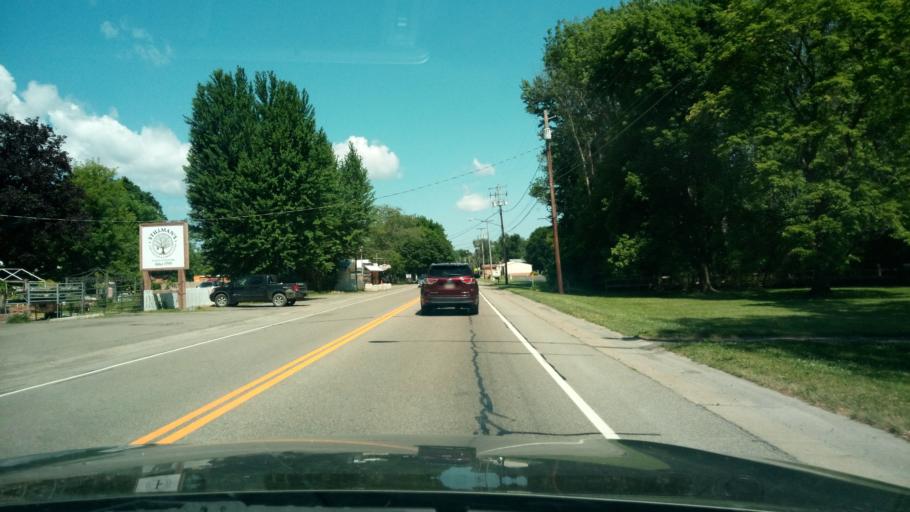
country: US
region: New York
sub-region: Schuyler County
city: Montour Falls
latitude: 42.3434
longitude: -76.8422
